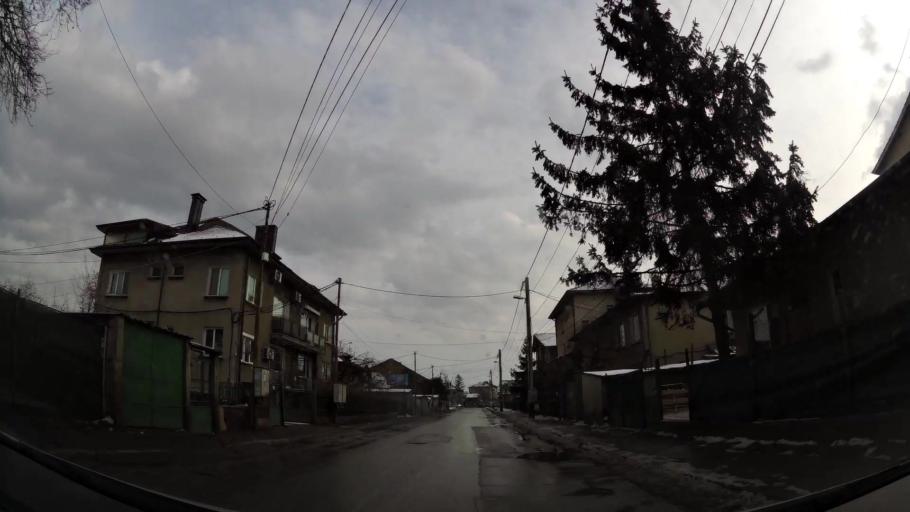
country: BG
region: Sofia-Capital
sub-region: Stolichna Obshtina
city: Sofia
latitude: 42.7060
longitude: 23.3840
